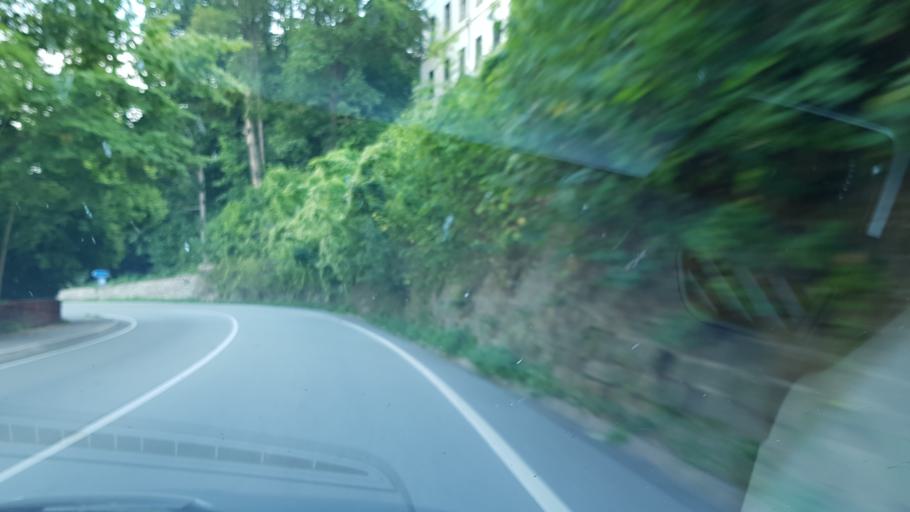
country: CZ
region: Pardubicky
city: Zamberk
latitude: 50.0861
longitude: 16.4677
